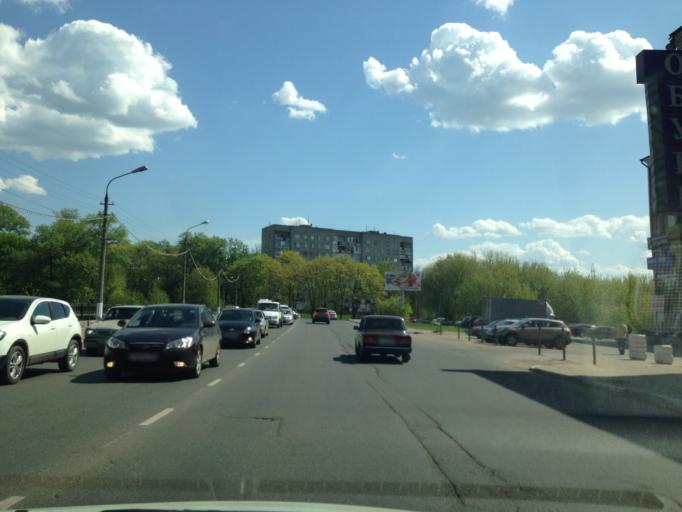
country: RU
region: Moskovskaya
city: Balashikha
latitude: 55.8137
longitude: 37.9570
